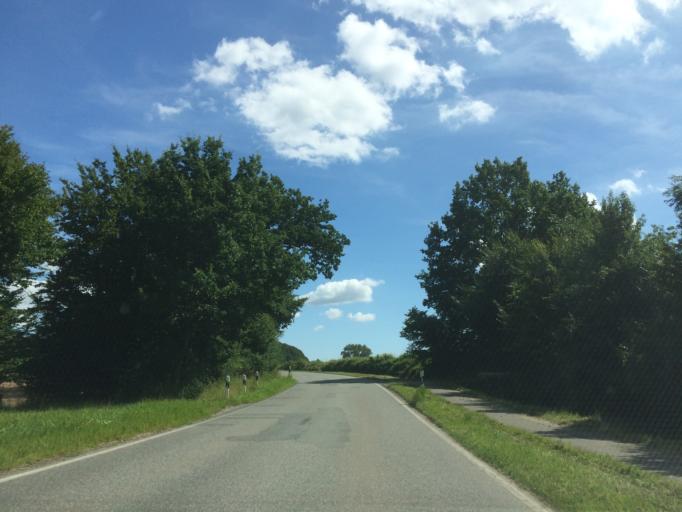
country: DE
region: Schleswig-Holstein
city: Grebin
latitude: 54.1950
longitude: 10.5117
